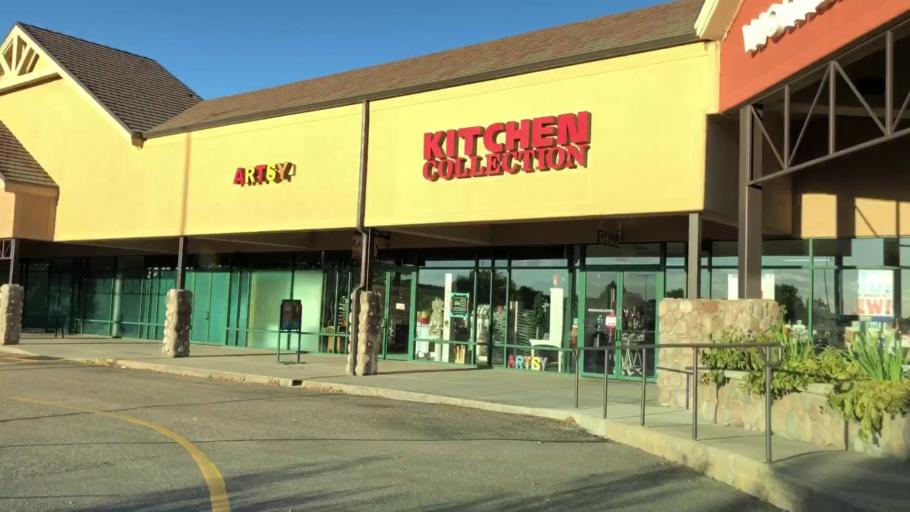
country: US
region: Colorado
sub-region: Larimer County
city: Loveland
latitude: 40.4127
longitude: -104.9966
